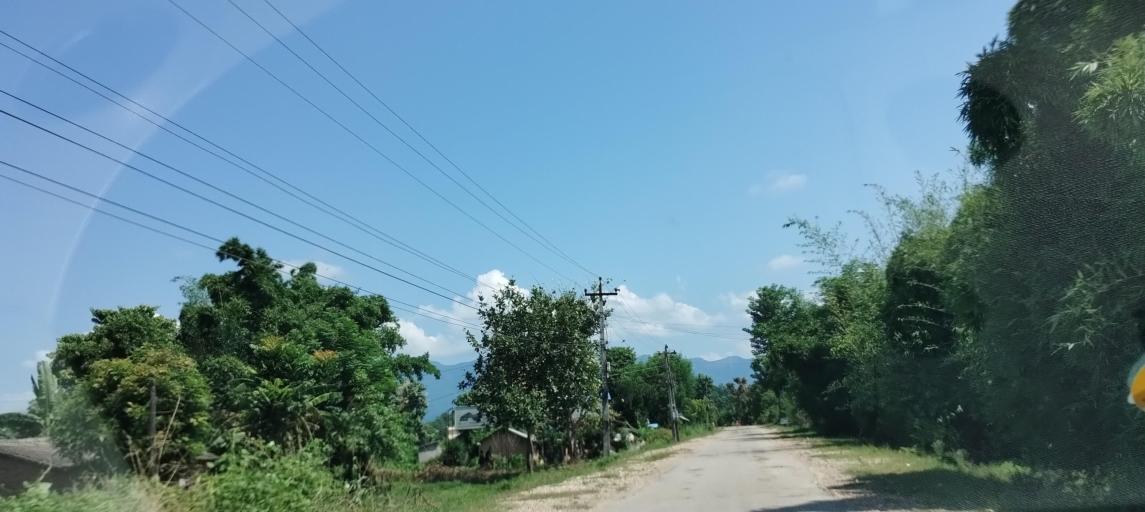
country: NP
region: Far Western
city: Tikapur
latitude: 28.5084
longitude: 81.3037
